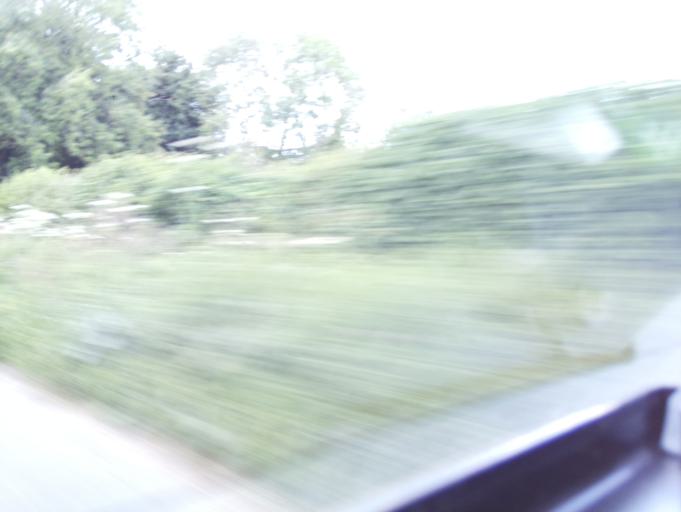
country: GB
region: England
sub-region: Gloucestershire
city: Chipping Campden
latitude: 52.0010
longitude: -1.7579
